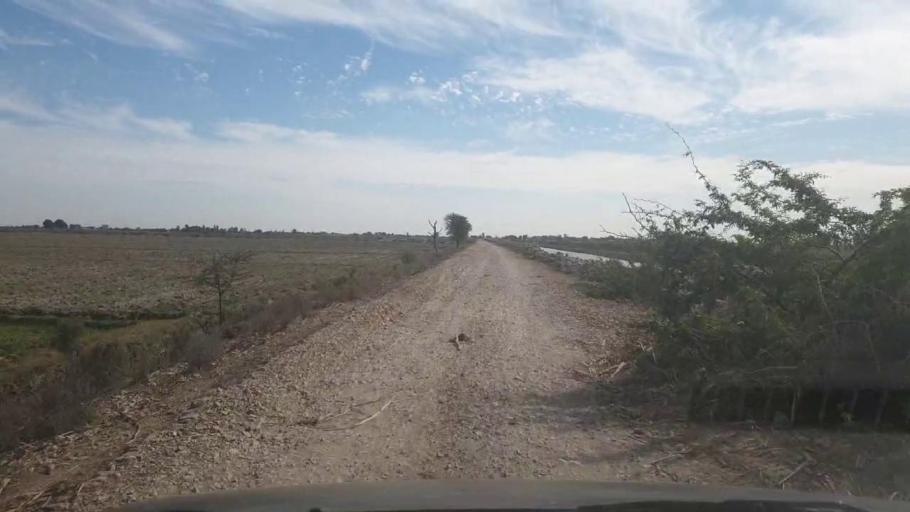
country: PK
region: Sindh
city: Mirwah Gorchani
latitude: 25.4283
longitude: 69.2003
